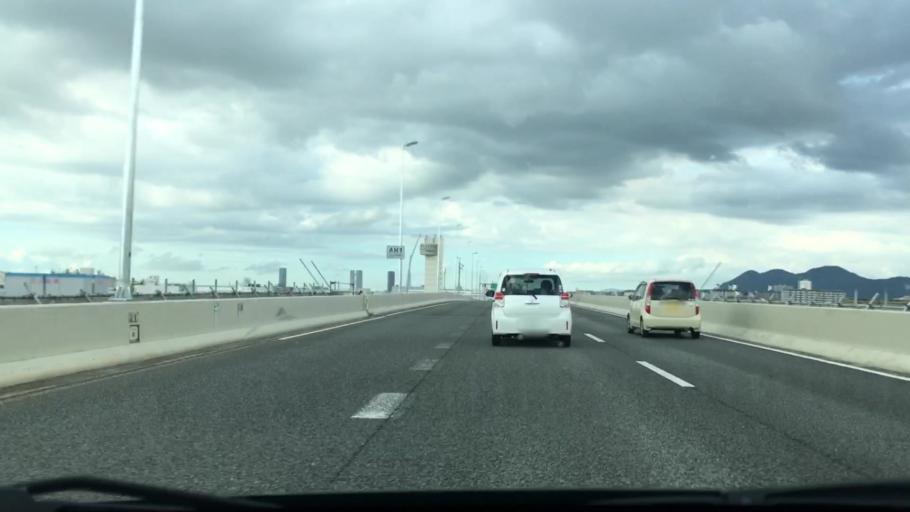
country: JP
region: Fukuoka
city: Fukuoka-shi
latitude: 33.6172
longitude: 130.4118
